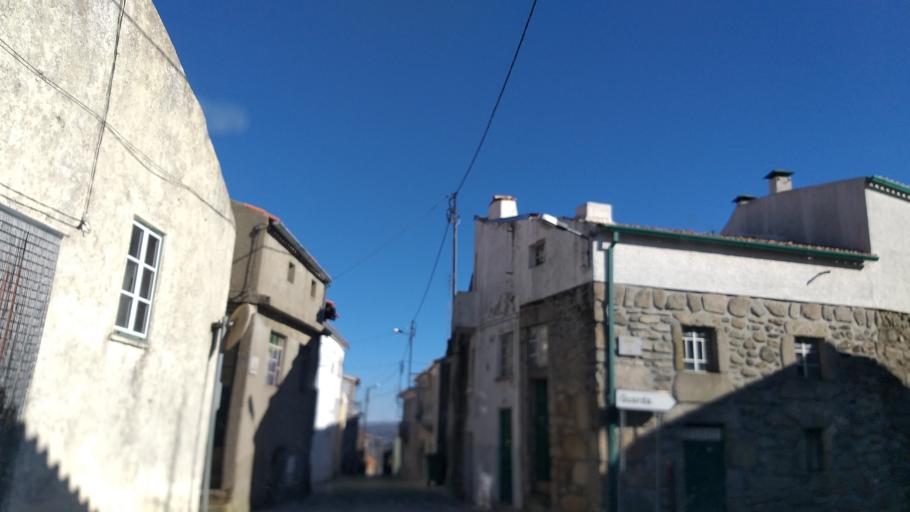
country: PT
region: Guarda
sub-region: Celorico da Beira
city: Celorico da Beira
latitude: 40.5145
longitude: -7.3922
